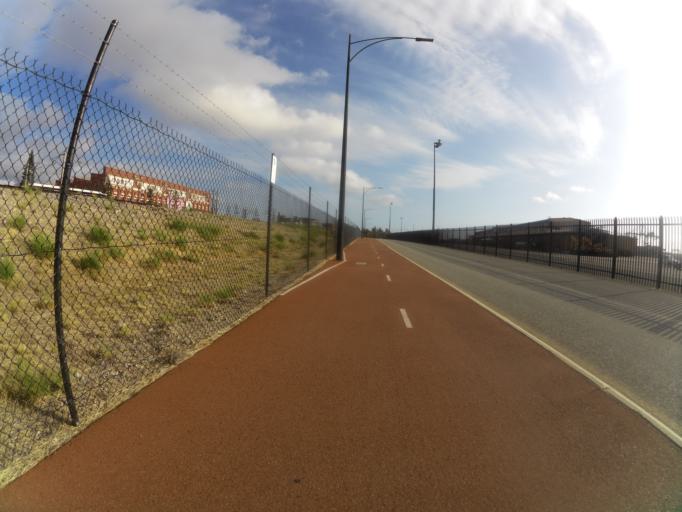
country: AU
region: Western Australia
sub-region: Fremantle
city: North Fremantle
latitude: -32.0461
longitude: 115.7500
